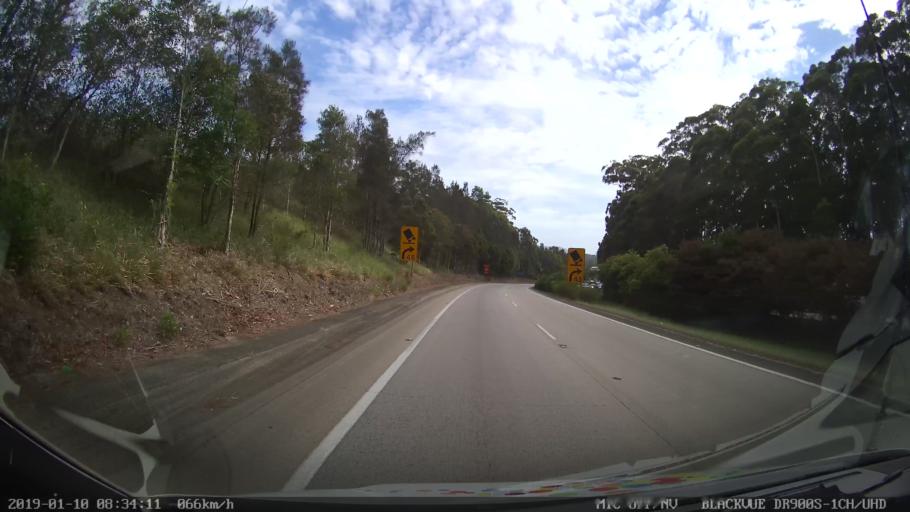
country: AU
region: New South Wales
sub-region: Coffs Harbour
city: Boambee
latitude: -30.3234
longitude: 153.0839
